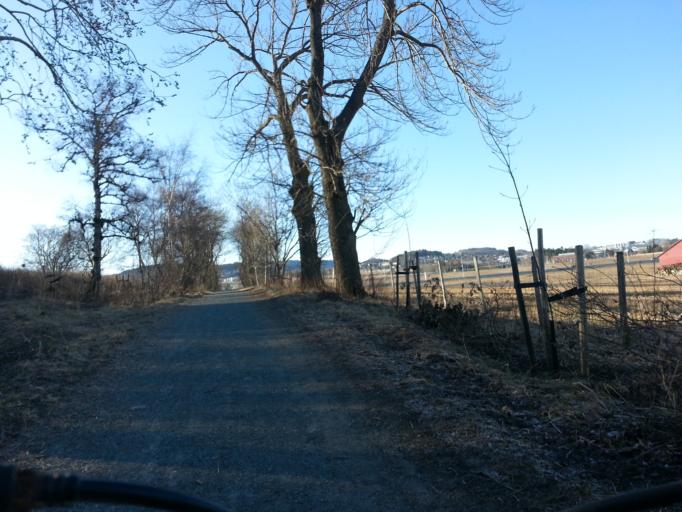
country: NO
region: Sor-Trondelag
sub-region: Trondheim
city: Trondheim
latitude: 63.4333
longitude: 10.4837
